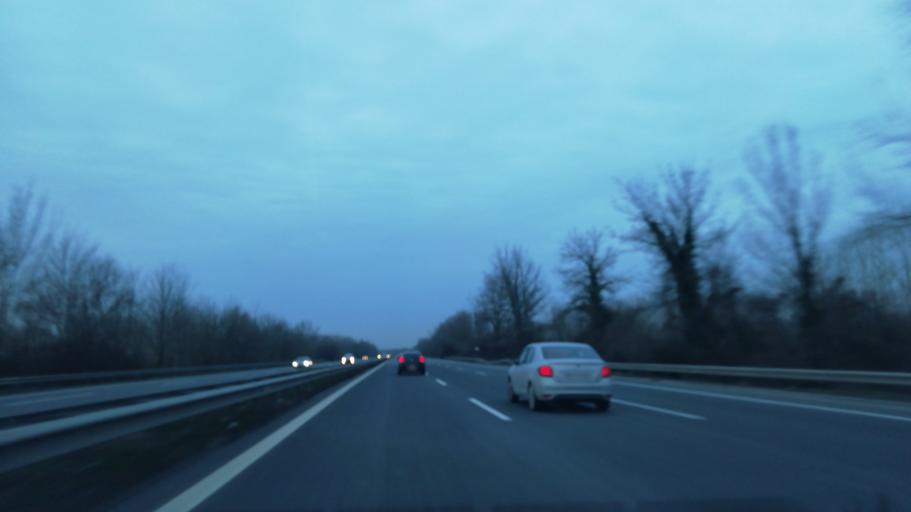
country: TR
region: Sakarya
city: Karapurcek
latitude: 40.7150
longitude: 30.4901
